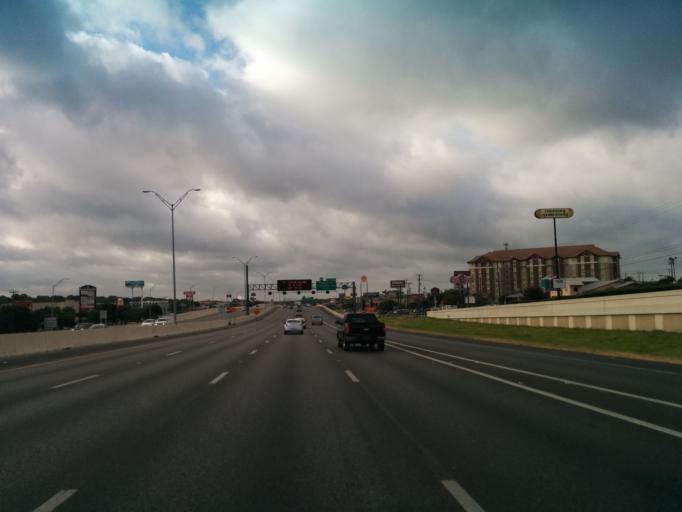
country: US
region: Texas
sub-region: Bexar County
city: Balcones Heights
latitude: 29.5334
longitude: -98.5647
